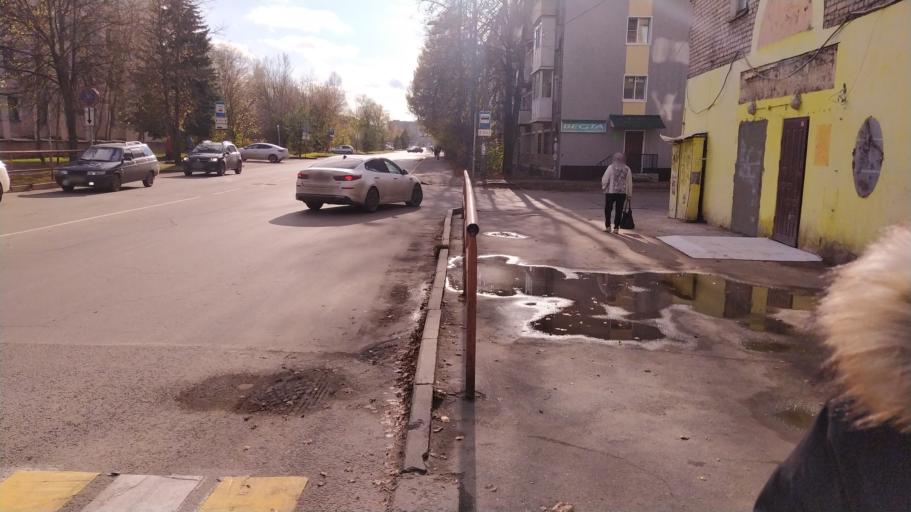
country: RU
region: Jaroslavl
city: Rybinsk
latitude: 58.0568
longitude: 38.7887
